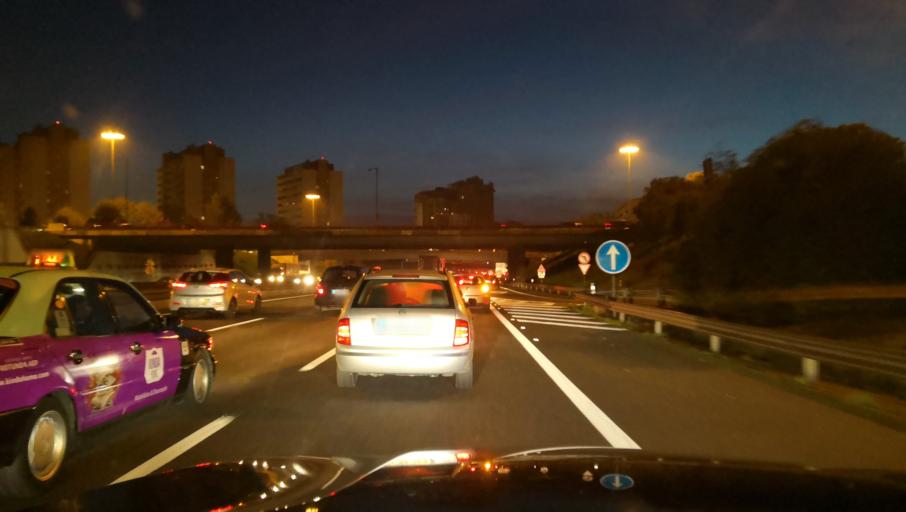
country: PT
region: Porto
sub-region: Matosinhos
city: Senhora da Hora
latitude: 41.1679
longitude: -8.6413
